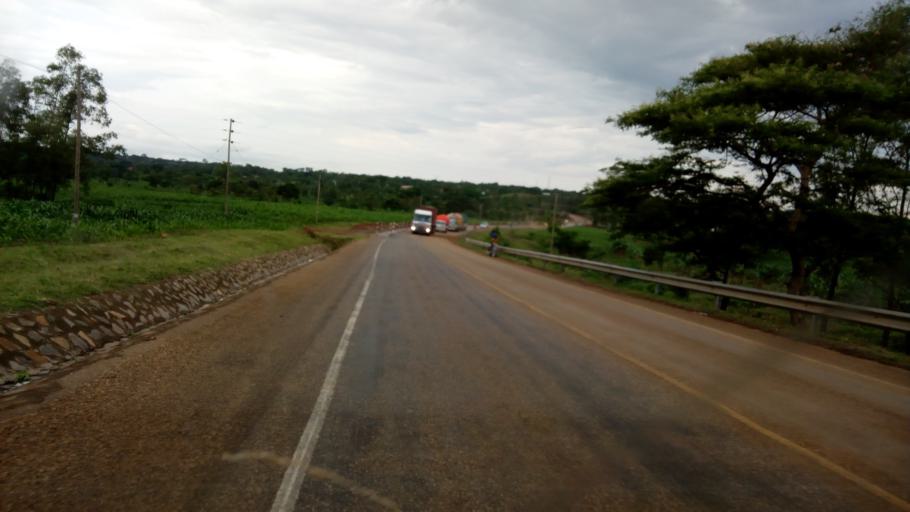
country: UG
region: Eastern Region
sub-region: Mbale District
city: Mbale
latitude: 0.9413
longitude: 34.1591
